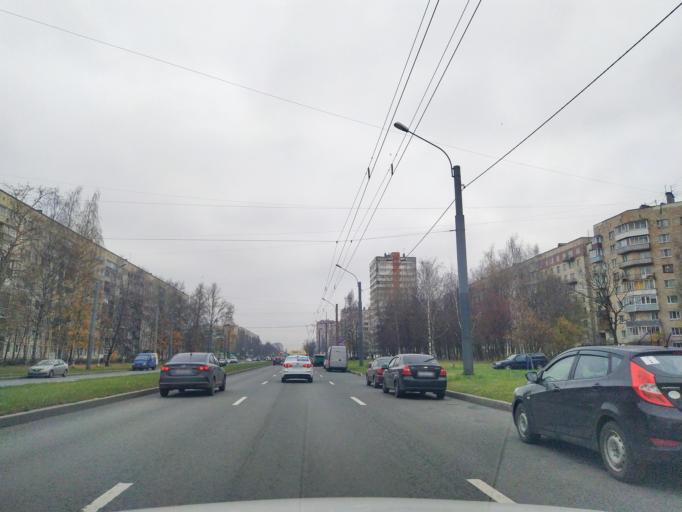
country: RU
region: St.-Petersburg
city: Sosnovka
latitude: 60.0409
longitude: 30.3479
